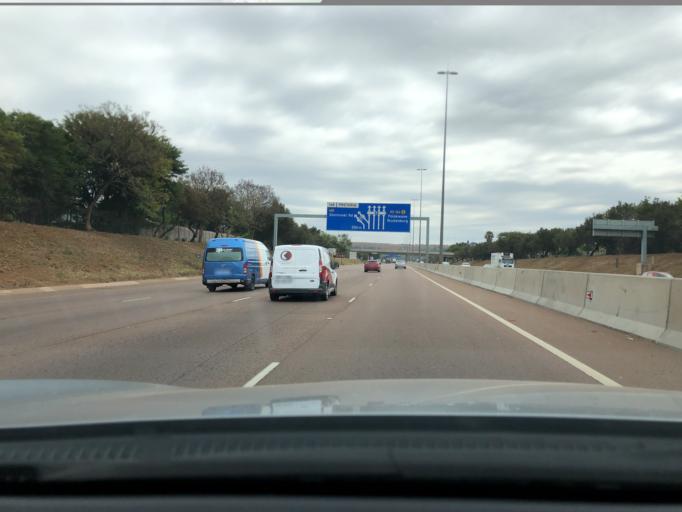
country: ZA
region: Gauteng
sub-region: City of Tshwane Metropolitan Municipality
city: Pretoria
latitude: -25.7239
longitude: 28.2652
